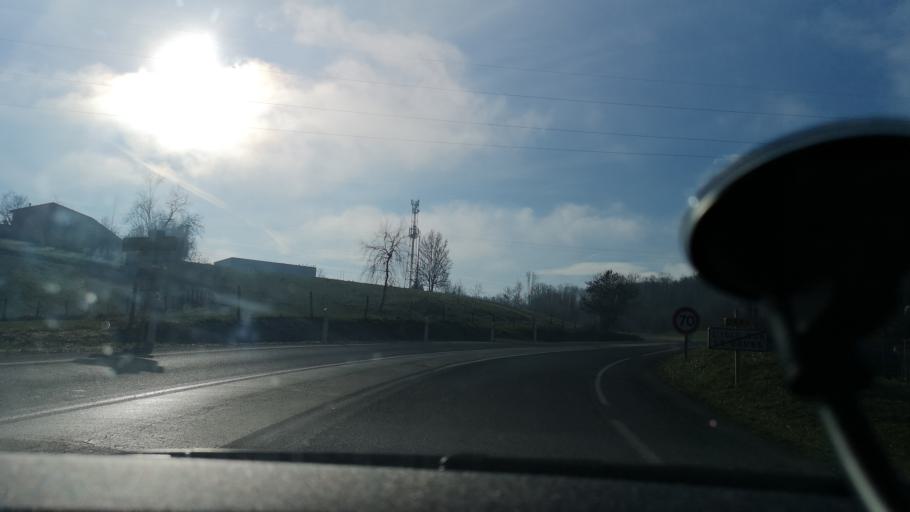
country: FR
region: Franche-Comte
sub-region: Departement du Doubs
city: Clerval
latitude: 47.4392
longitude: 6.5805
